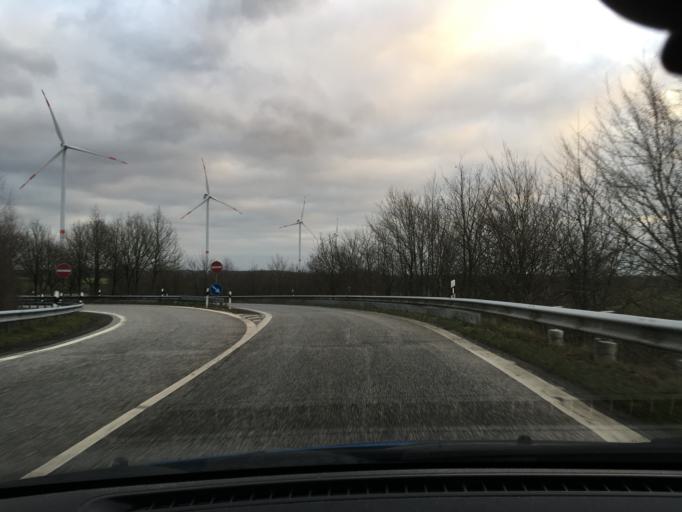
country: DE
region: Schleswig-Holstein
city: Tensbuttel-Rost
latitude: 54.1150
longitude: 9.2579
